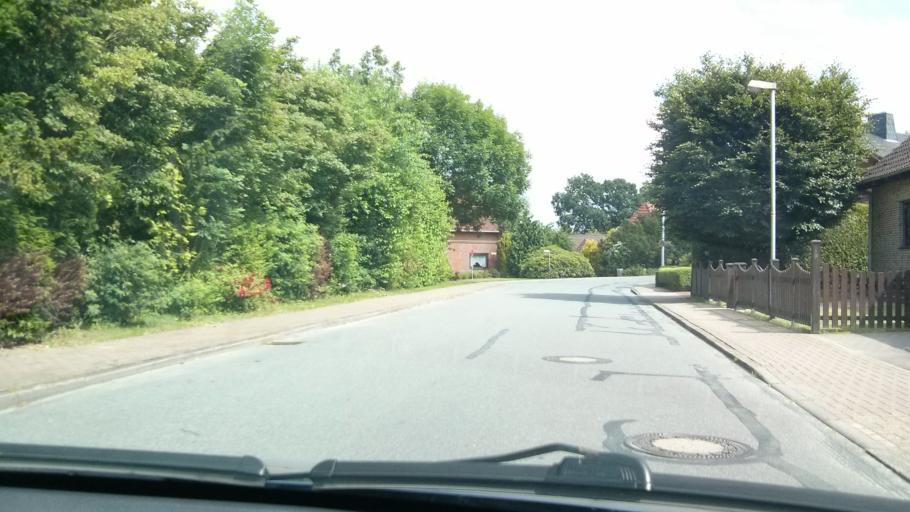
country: DE
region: Lower Saxony
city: Schiffdorf
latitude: 53.5305
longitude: 8.6545
